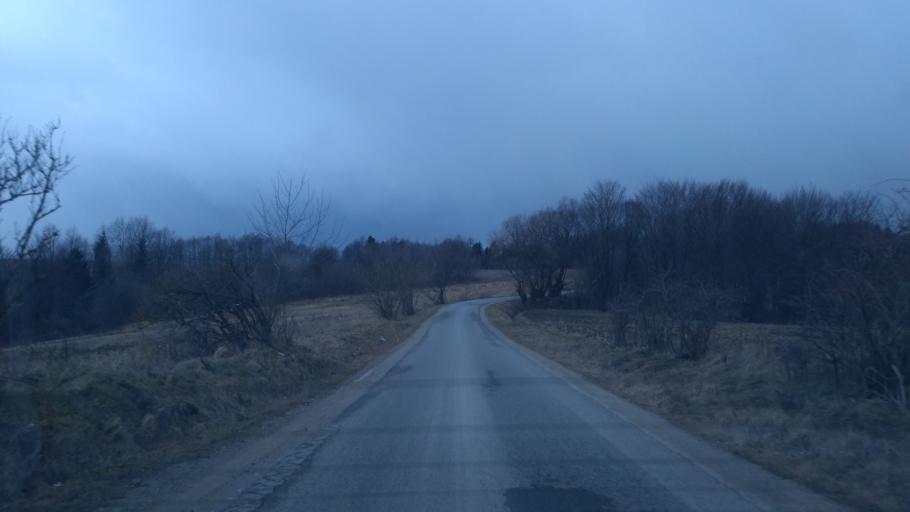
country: PL
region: Subcarpathian Voivodeship
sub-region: Powiat rzeszowski
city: Blazowa
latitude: 49.8890
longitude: 22.1408
